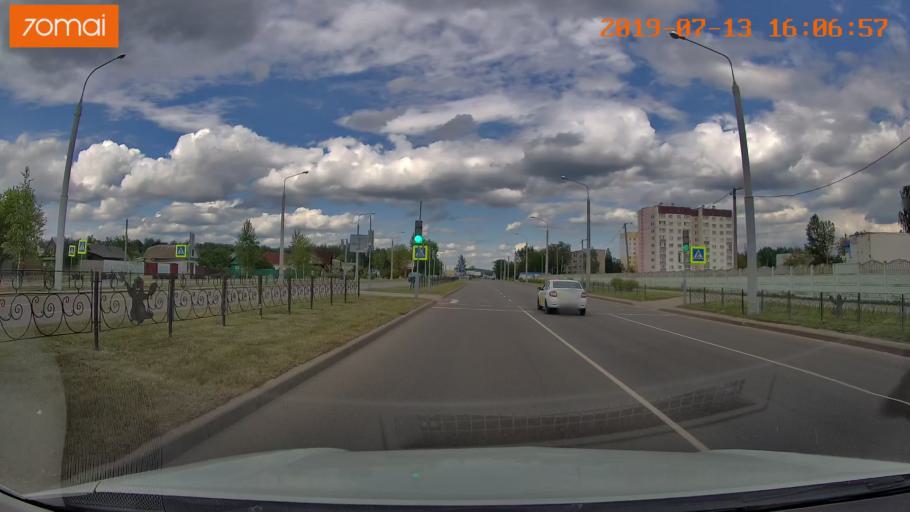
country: BY
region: Mogilev
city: Babruysk
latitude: 53.1550
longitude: 29.2093
